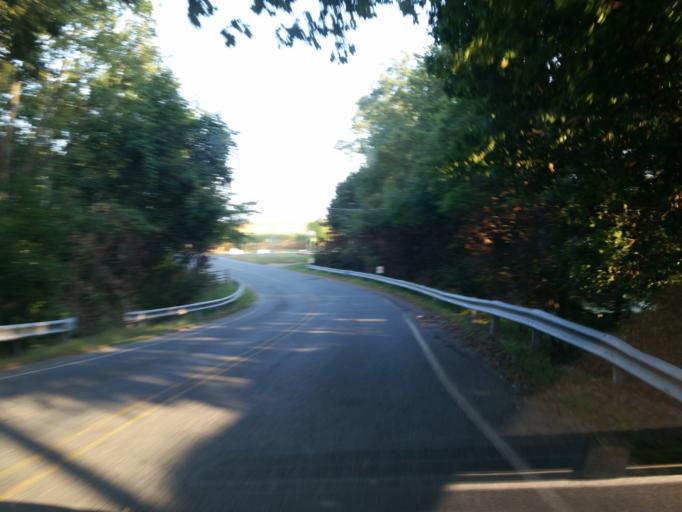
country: US
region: Pennsylvania
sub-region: Lebanon County
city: Annville
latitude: 40.3637
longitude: -76.5049
